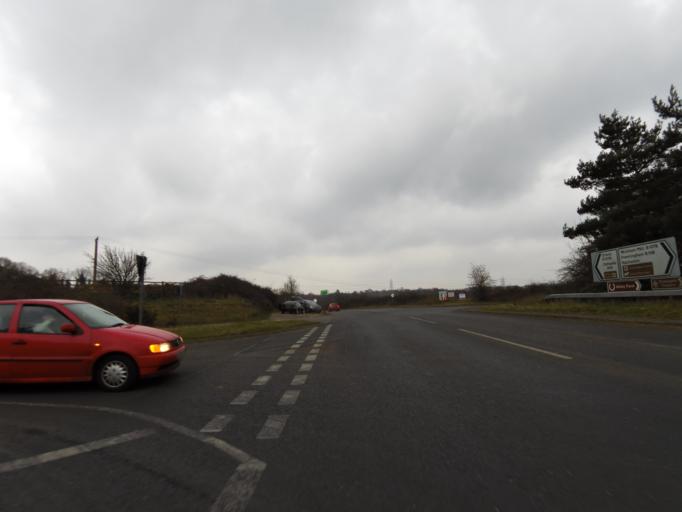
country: GB
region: England
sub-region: Suffolk
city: Wickham Market
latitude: 52.1597
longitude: 1.3805
